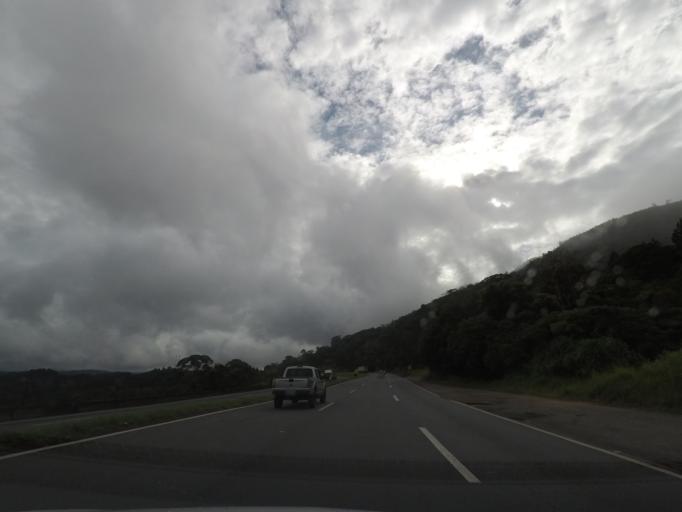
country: BR
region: Parana
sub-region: Campina Grande Do Sul
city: Campina Grande do Sul
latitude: -25.1533
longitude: -48.8606
